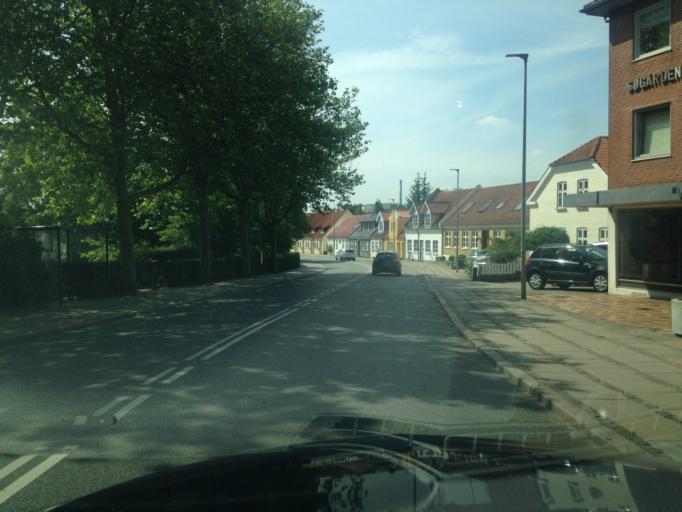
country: DK
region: South Denmark
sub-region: Kolding Kommune
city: Kolding
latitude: 55.4954
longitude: 9.4710
